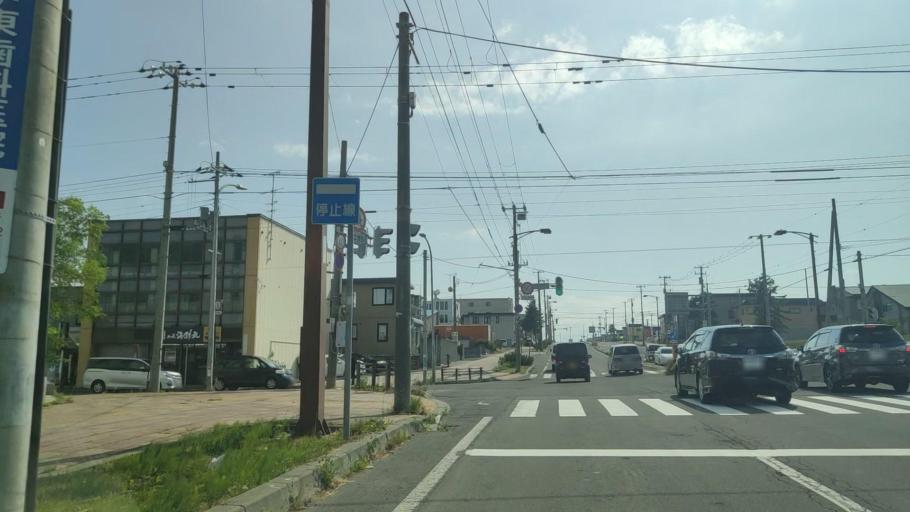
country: JP
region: Hokkaido
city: Rumoi
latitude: 43.9412
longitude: 141.6405
